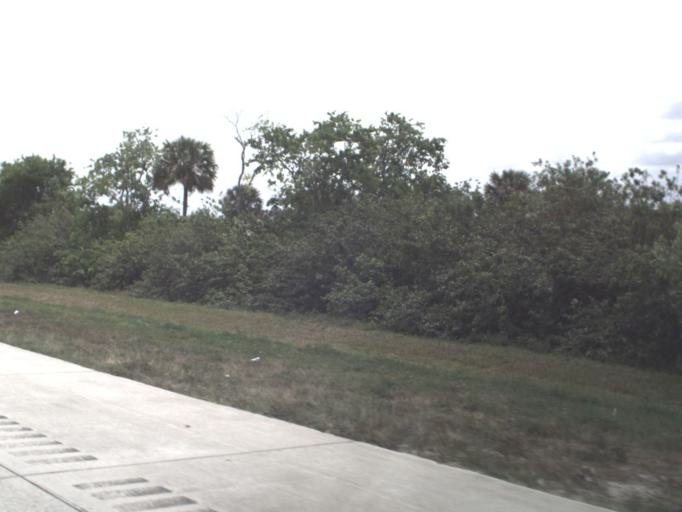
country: US
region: Florida
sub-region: Brevard County
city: Cocoa West
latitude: 28.3402
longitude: -80.7819
